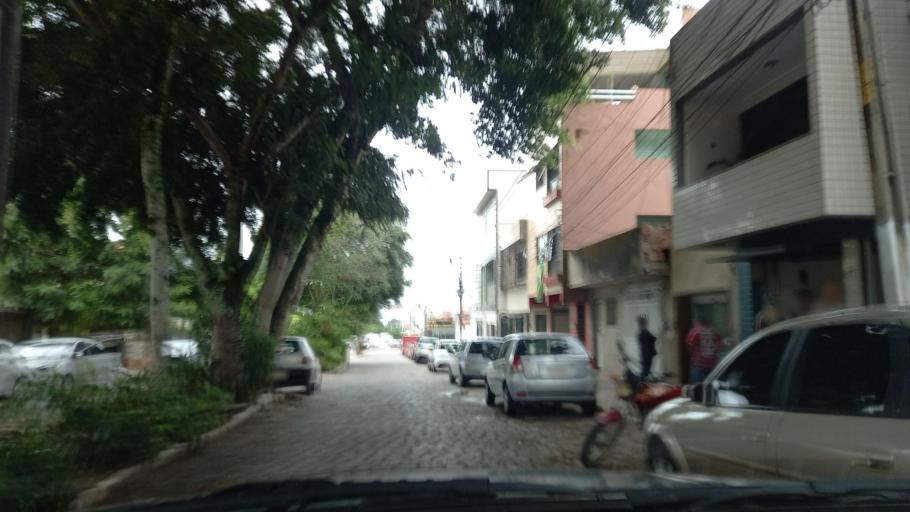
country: BR
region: Pernambuco
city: Garanhuns
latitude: -8.8831
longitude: -36.4815
